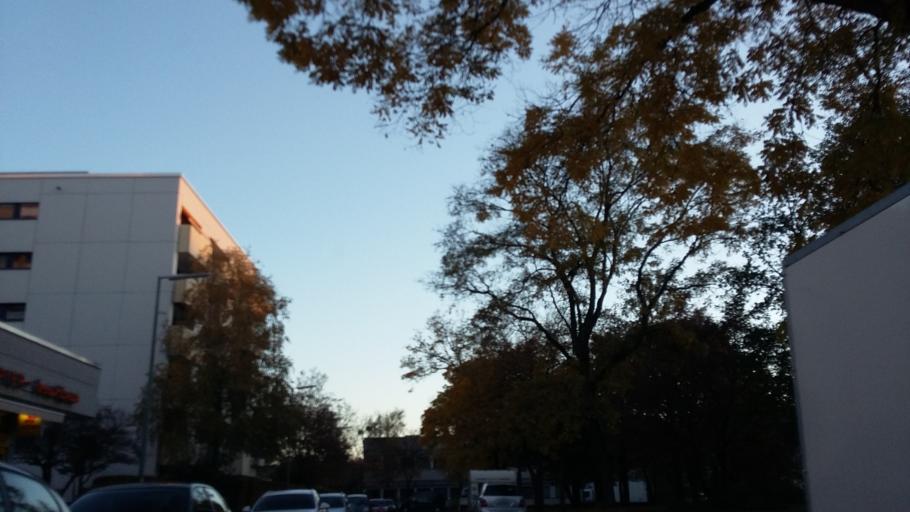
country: DE
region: Bavaria
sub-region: Upper Bavaria
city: Pasing
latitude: 48.1292
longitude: 11.5080
